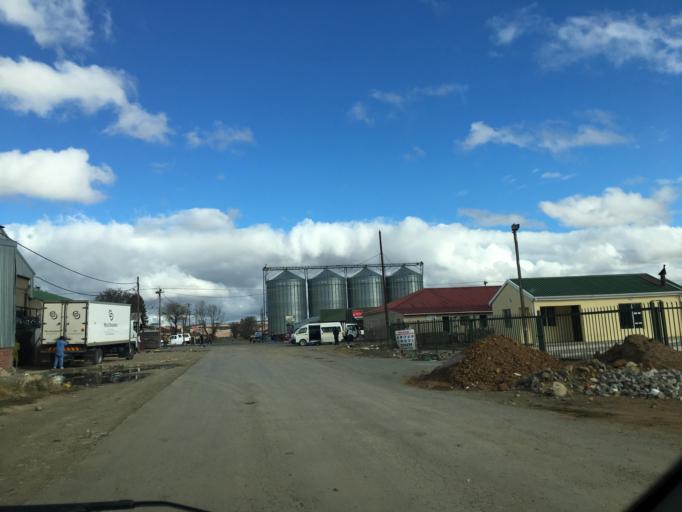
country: ZA
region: Eastern Cape
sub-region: Chris Hani District Municipality
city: Elliot
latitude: -31.3341
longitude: 27.8467
